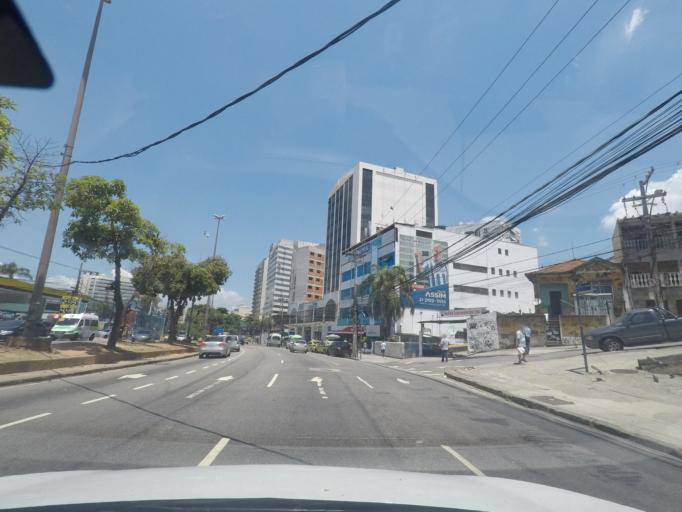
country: BR
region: Rio de Janeiro
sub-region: Rio De Janeiro
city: Rio de Janeiro
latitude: -22.8875
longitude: -43.2859
